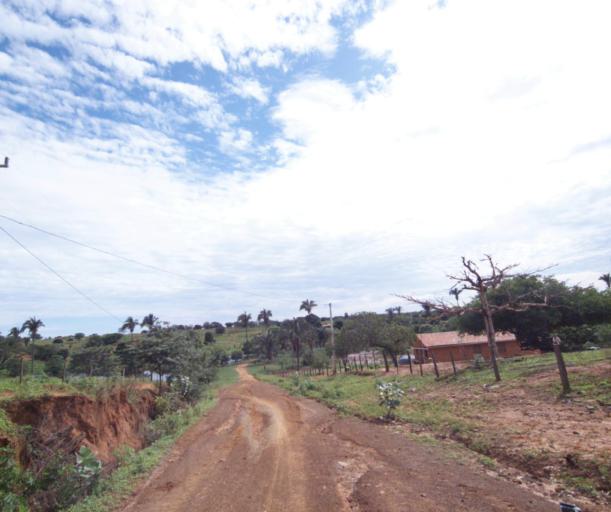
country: BR
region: Bahia
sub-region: Carinhanha
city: Carinhanha
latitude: -14.2377
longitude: -44.4080
